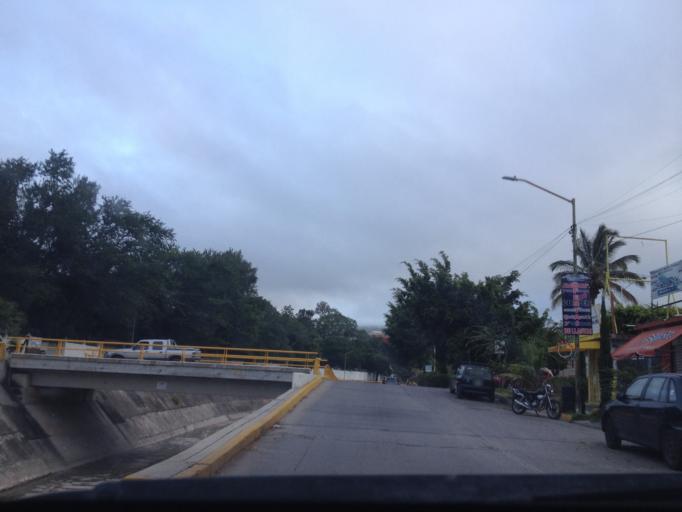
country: MX
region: Guerrero
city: Chilpancingo de los Bravos
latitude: 17.5464
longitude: -99.5024
